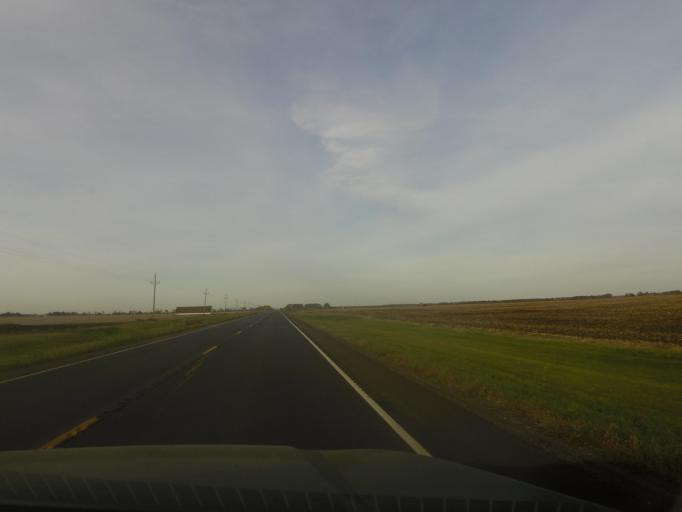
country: US
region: North Dakota
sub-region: Pembina County
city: Cavalier
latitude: 48.8046
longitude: -97.5217
